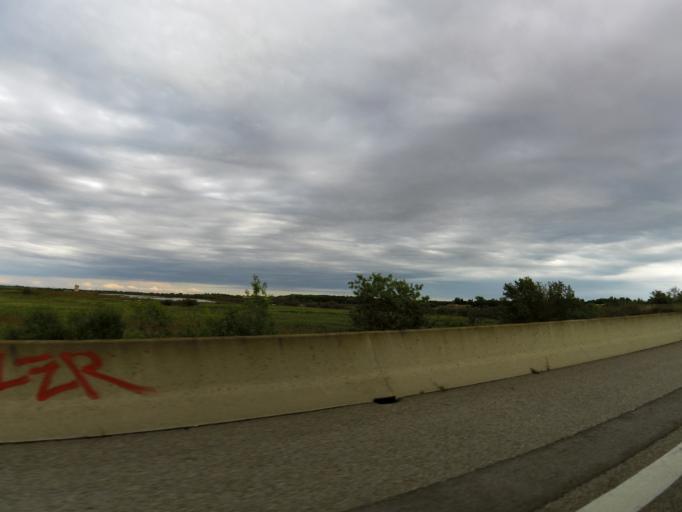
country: FR
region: Languedoc-Roussillon
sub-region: Departement du Gard
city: Aigues-Mortes
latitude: 43.5904
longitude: 4.1961
